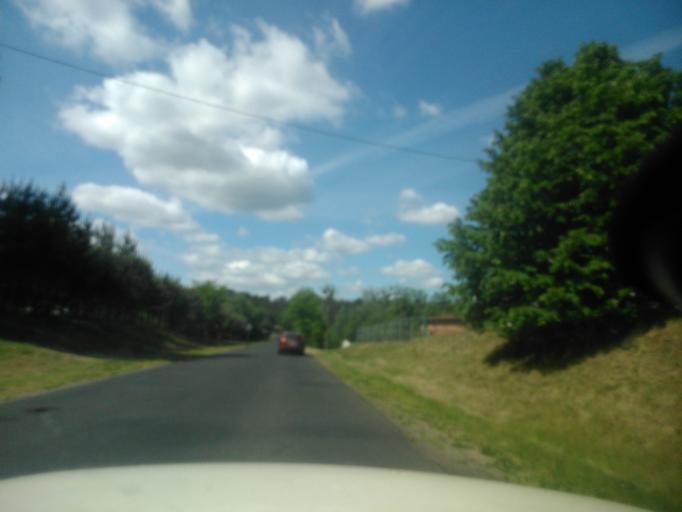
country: PL
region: Kujawsko-Pomorskie
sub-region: Powiat golubsko-dobrzynski
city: Golub-Dobrzyn
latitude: 53.0932
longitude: 18.9979
